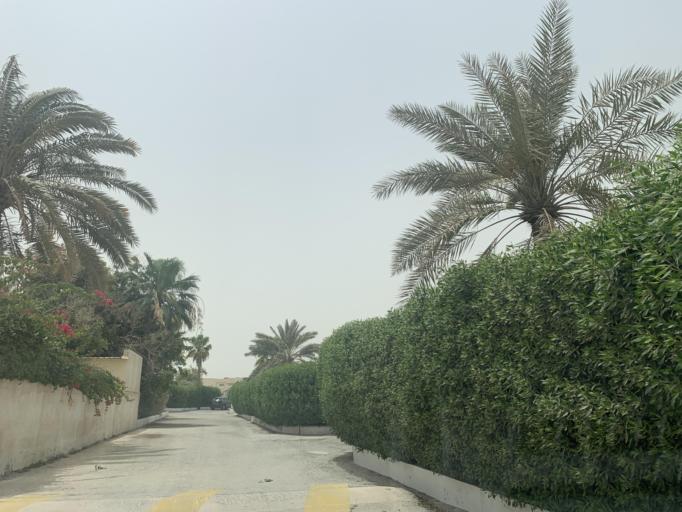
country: BH
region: Manama
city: Jidd Hafs
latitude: 26.2287
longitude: 50.5192
